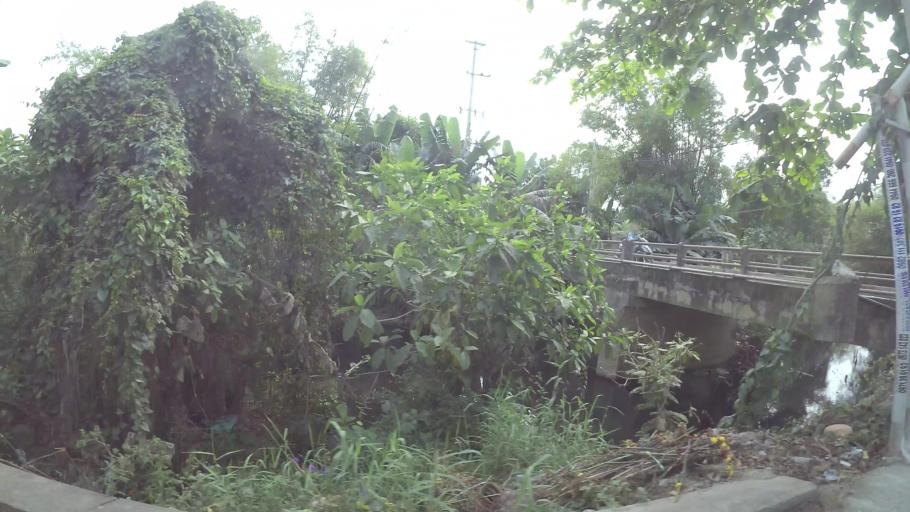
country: VN
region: Da Nang
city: Lien Chieu
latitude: 16.0592
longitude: 108.1571
